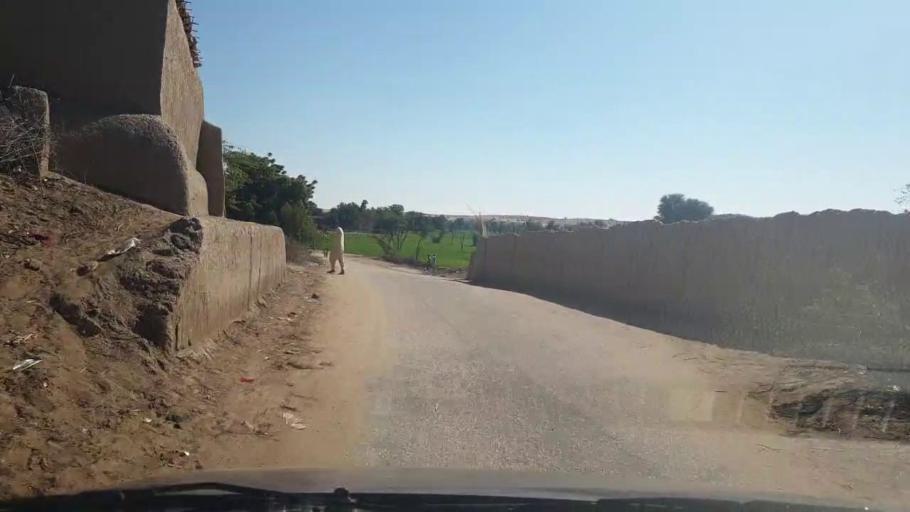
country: PK
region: Sindh
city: Bozdar
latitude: 27.0515
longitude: 68.6491
